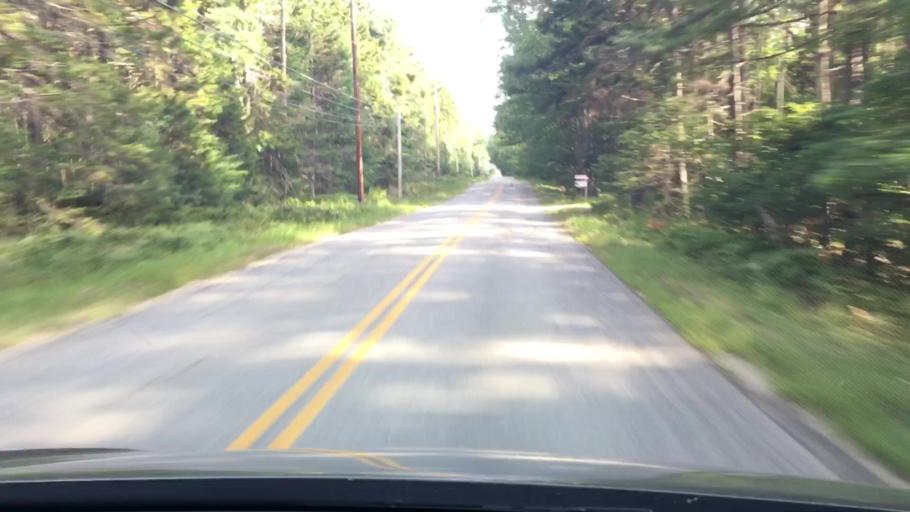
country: US
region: Maine
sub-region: Hancock County
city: Bucksport
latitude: 44.5359
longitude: -68.7939
